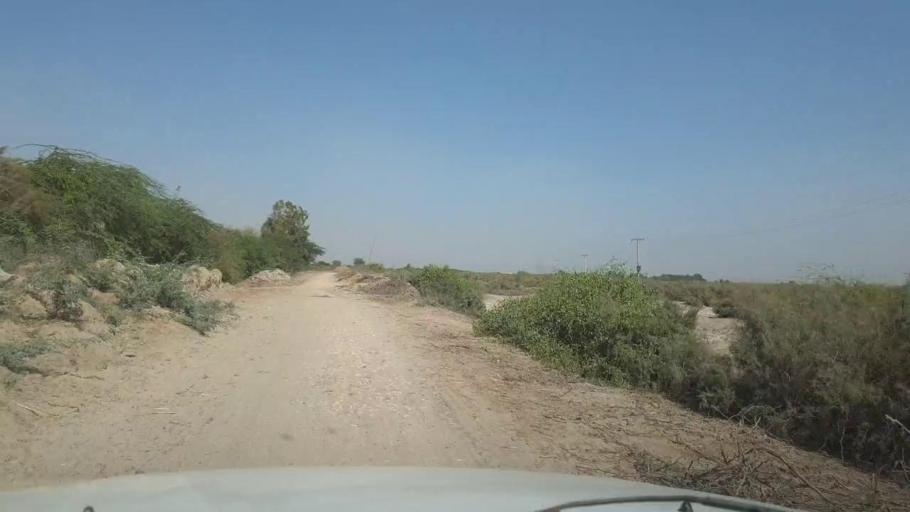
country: PK
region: Sindh
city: Mirpur Sakro
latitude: 24.3983
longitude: 67.7570
